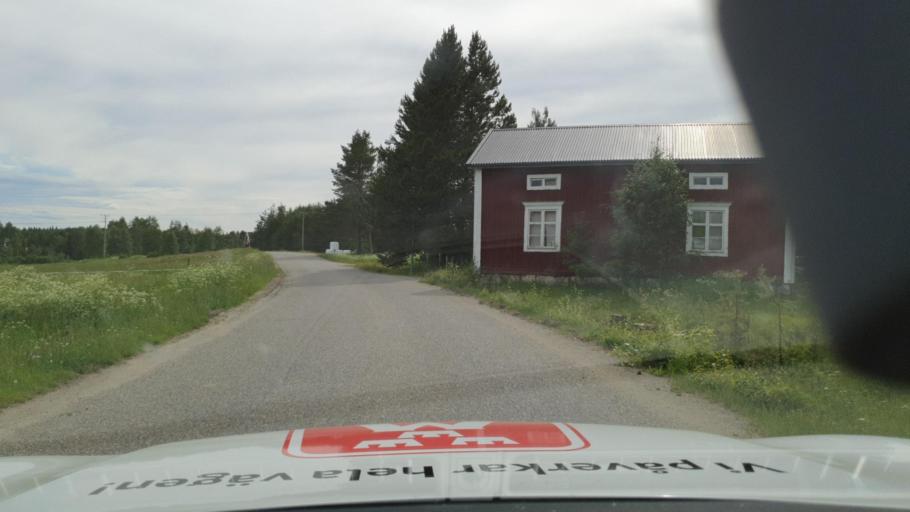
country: SE
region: Vaesterbotten
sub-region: Robertsfors Kommun
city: Robertsfors
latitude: 64.3980
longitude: 21.0198
